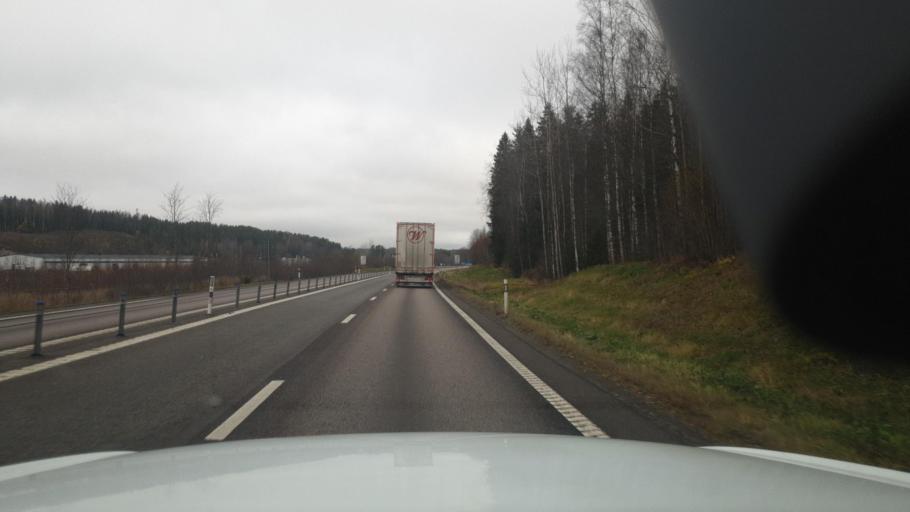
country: SE
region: Vaermland
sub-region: Arvika Kommun
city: Arvika
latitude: 59.6565
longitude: 12.6513
